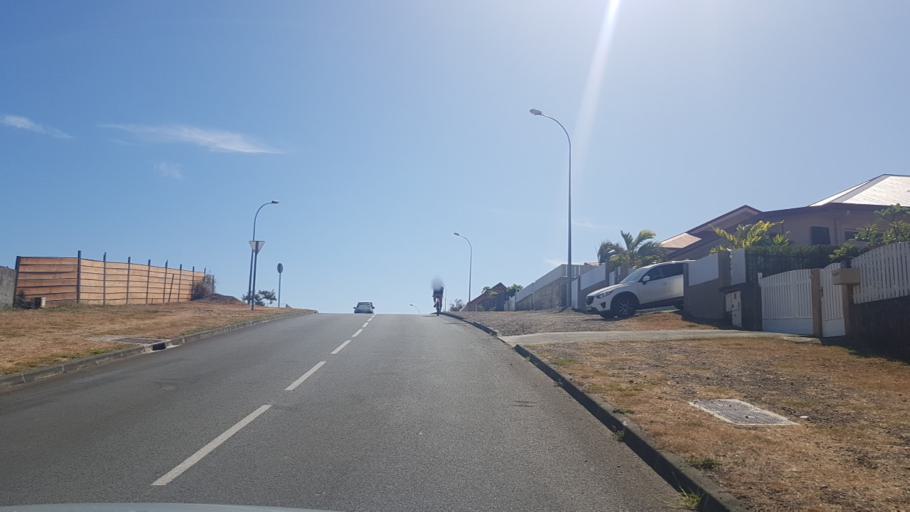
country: NC
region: South Province
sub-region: Dumbea
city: Dumbea
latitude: -22.1950
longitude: 166.4419
